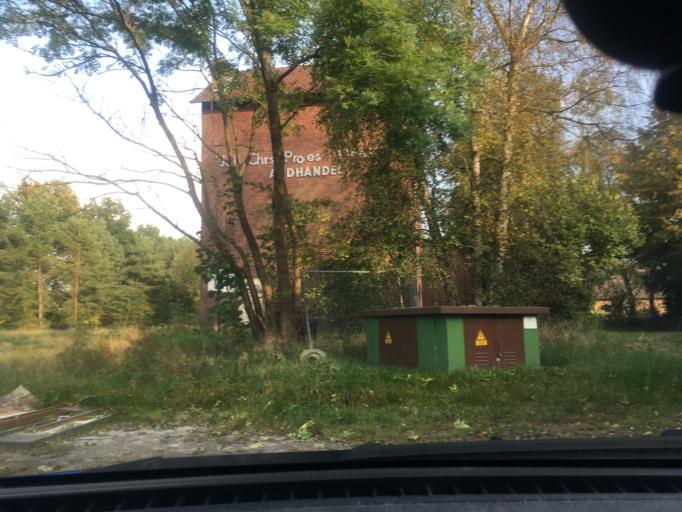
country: DE
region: Lower Saxony
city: Vastorf
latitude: 53.1988
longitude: 10.5557
